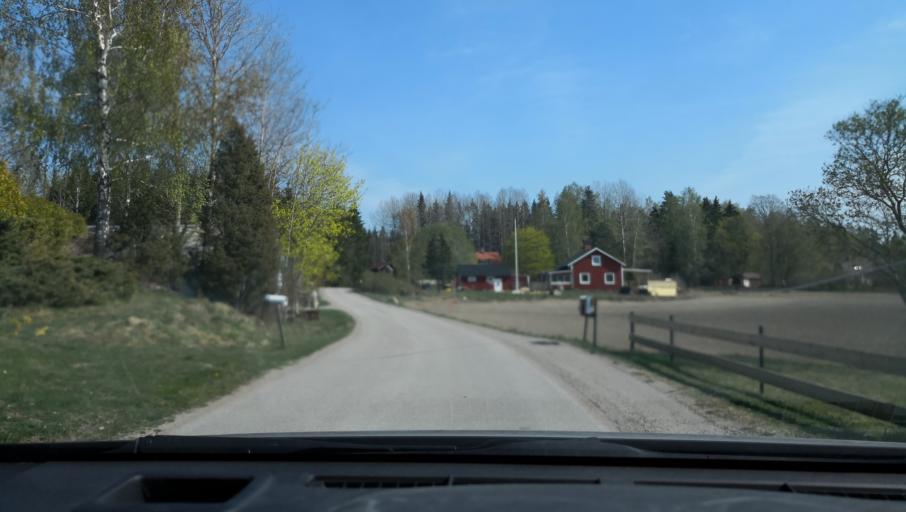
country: SE
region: Vaestmanland
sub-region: Sala Kommun
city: Sala
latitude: 60.0069
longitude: 16.7084
